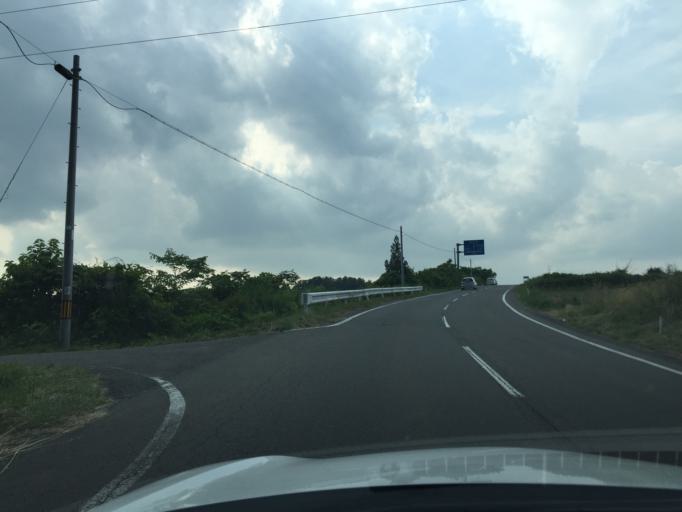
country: JP
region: Fukushima
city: Miharu
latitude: 37.3975
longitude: 140.4481
